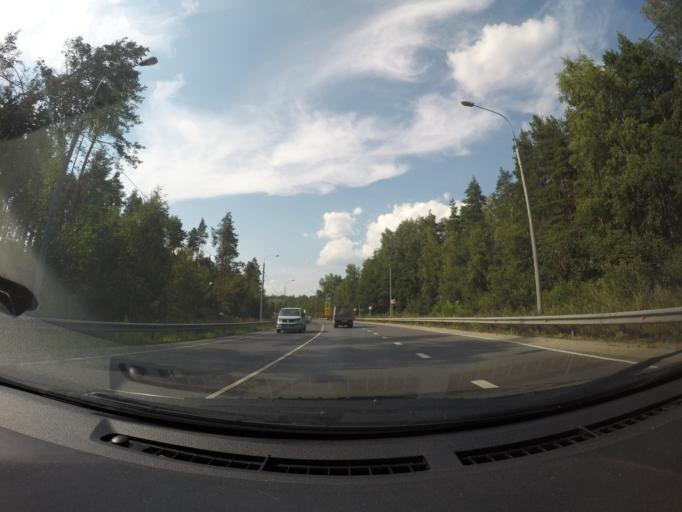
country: RU
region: Moskovskaya
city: Ramenskoye
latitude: 55.6326
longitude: 38.2780
